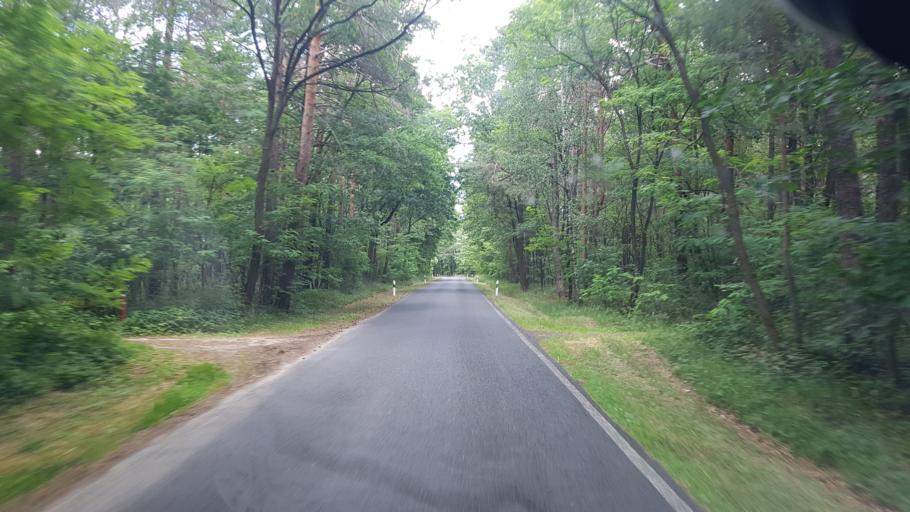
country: DE
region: Brandenburg
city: Sallgast
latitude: 51.5808
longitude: 13.9151
